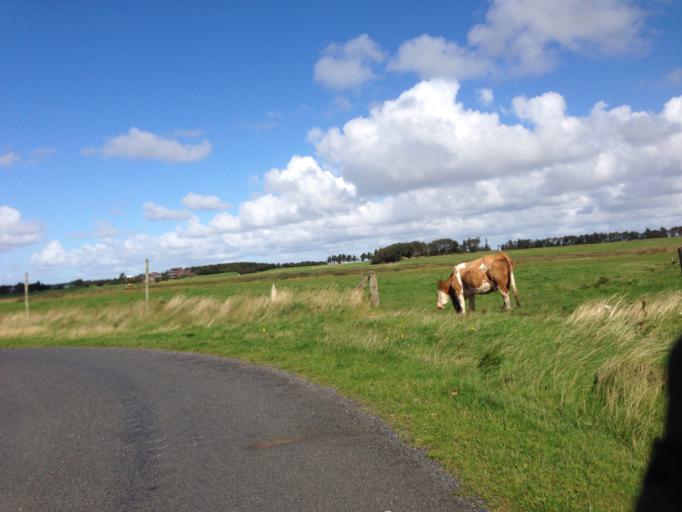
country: DE
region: Schleswig-Holstein
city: Witsum
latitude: 54.6992
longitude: 8.4266
